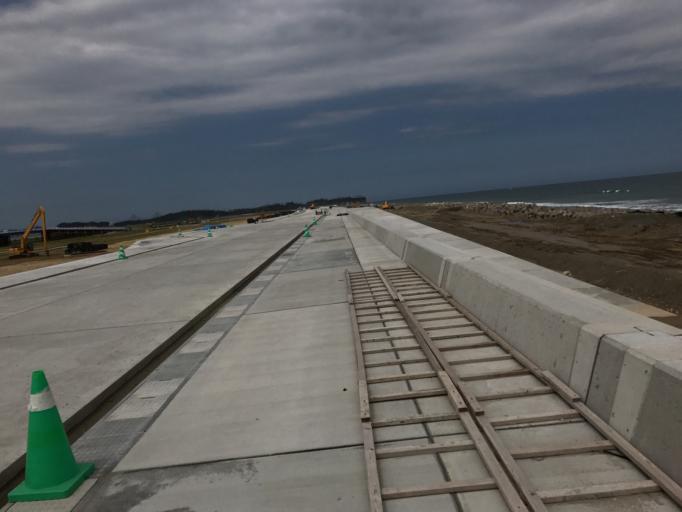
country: JP
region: Miyagi
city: Marumori
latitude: 37.8019
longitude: 140.9859
